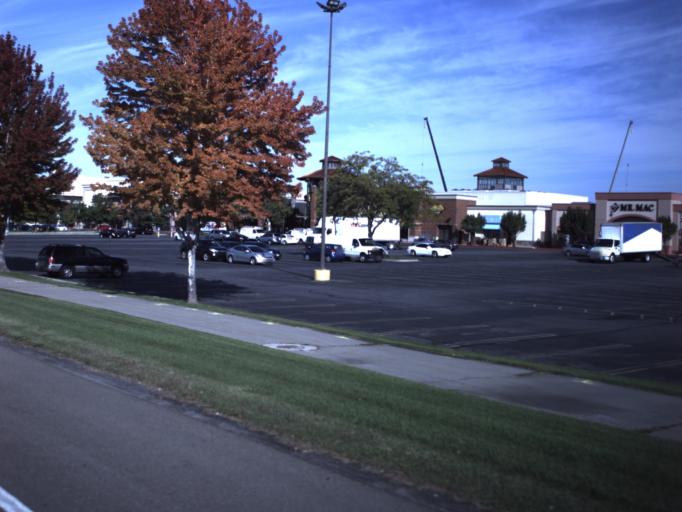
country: US
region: Utah
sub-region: Utah County
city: Orem
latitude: 40.2734
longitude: -111.6801
